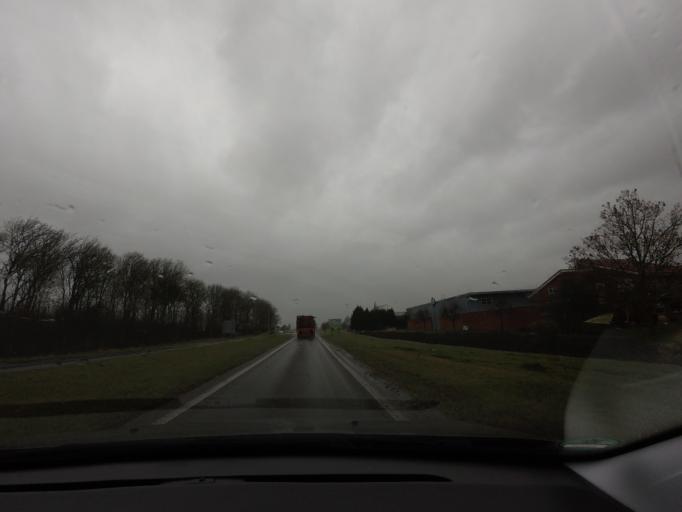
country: NL
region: Friesland
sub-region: Sudwest Fryslan
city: Bolsward
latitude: 53.0636
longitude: 5.5092
